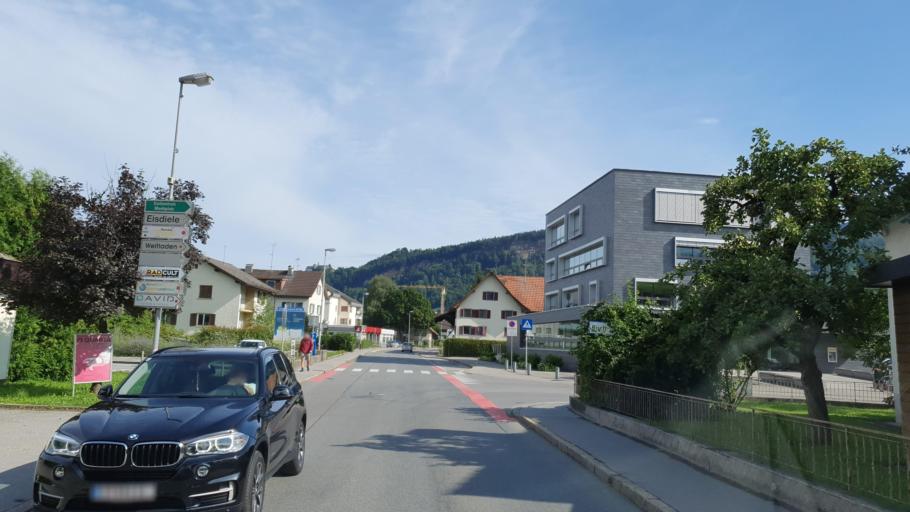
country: AT
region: Vorarlberg
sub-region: Politischer Bezirk Bregenz
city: Wolfurt
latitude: 47.4732
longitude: 9.7504
